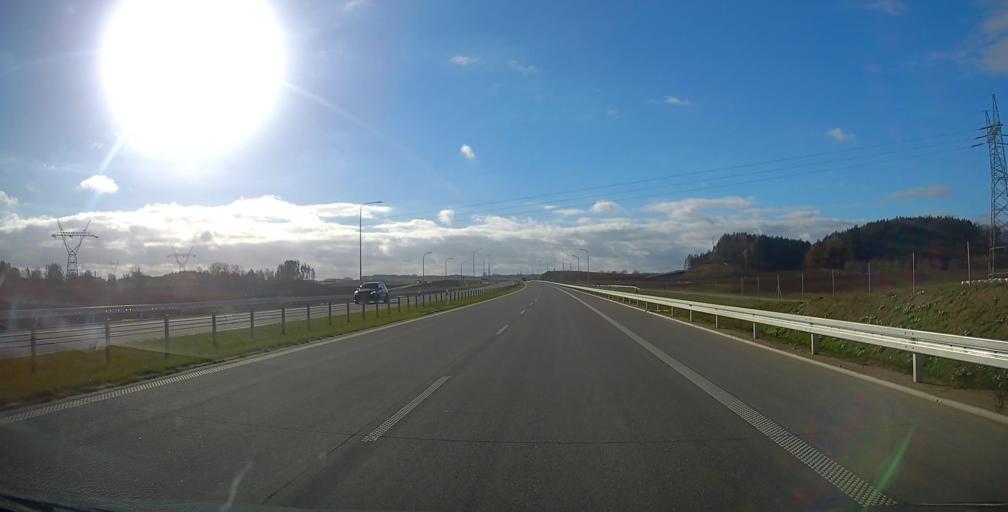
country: PL
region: Warmian-Masurian Voivodeship
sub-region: Powiat elcki
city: Elk
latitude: 53.7472
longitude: 22.3082
